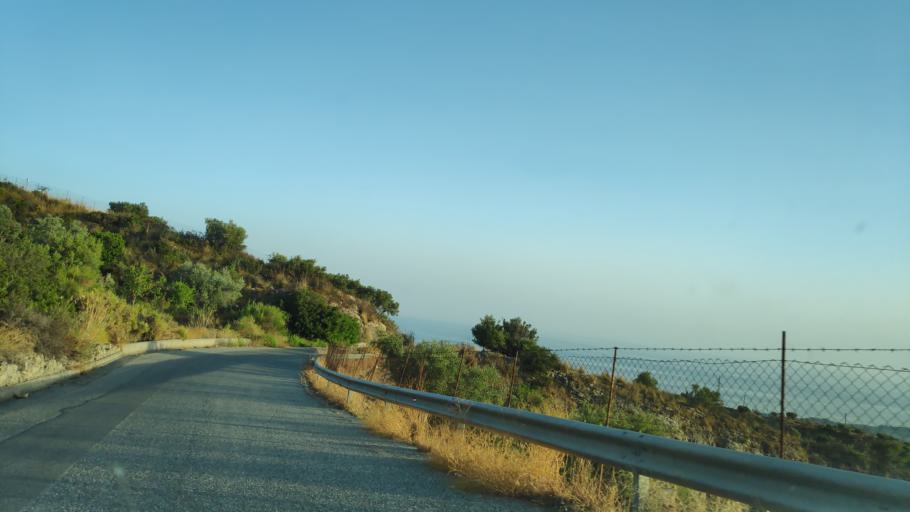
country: IT
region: Calabria
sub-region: Provincia di Reggio Calabria
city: Bova Marina
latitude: 37.9630
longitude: 15.9206
